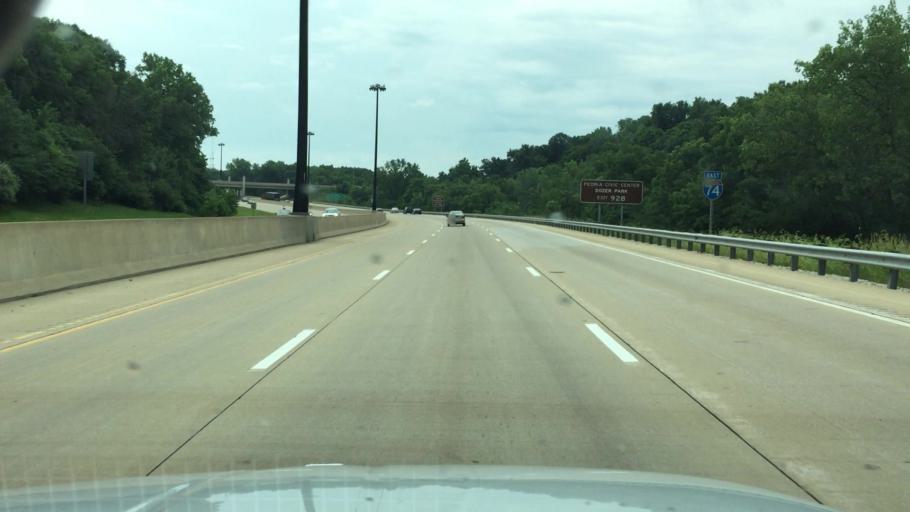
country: US
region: Illinois
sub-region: Peoria County
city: West Peoria
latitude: 40.7142
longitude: -89.6217
